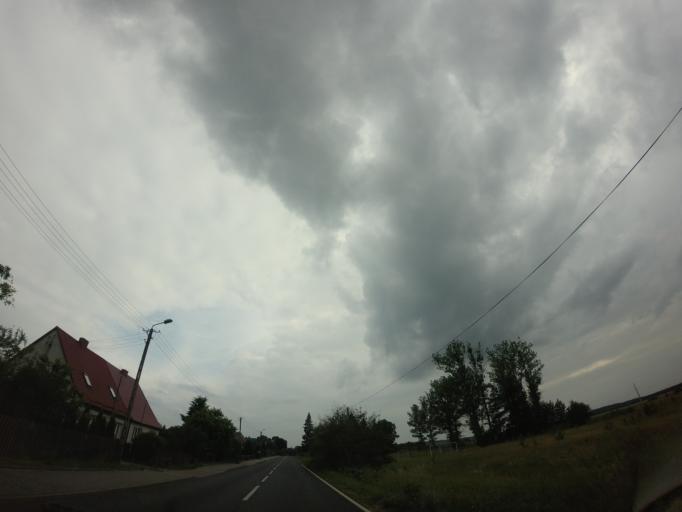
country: PL
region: West Pomeranian Voivodeship
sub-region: Powiat drawski
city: Wierzchowo
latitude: 53.4372
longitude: 16.2054
